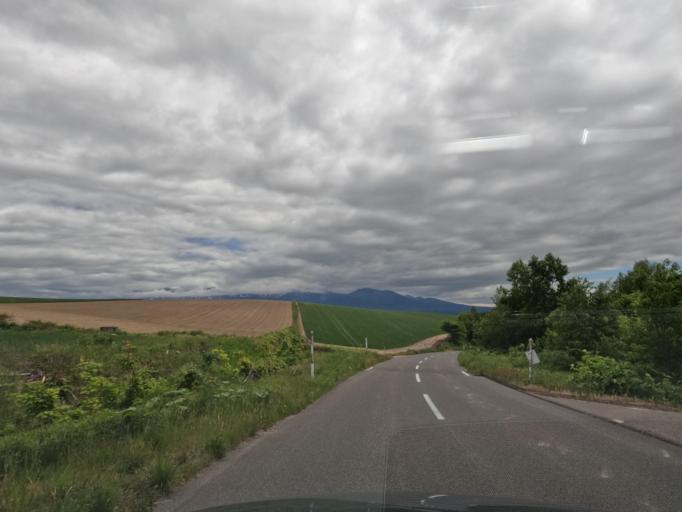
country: JP
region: Hokkaido
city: Shimo-furano
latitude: 43.4989
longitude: 142.4148
